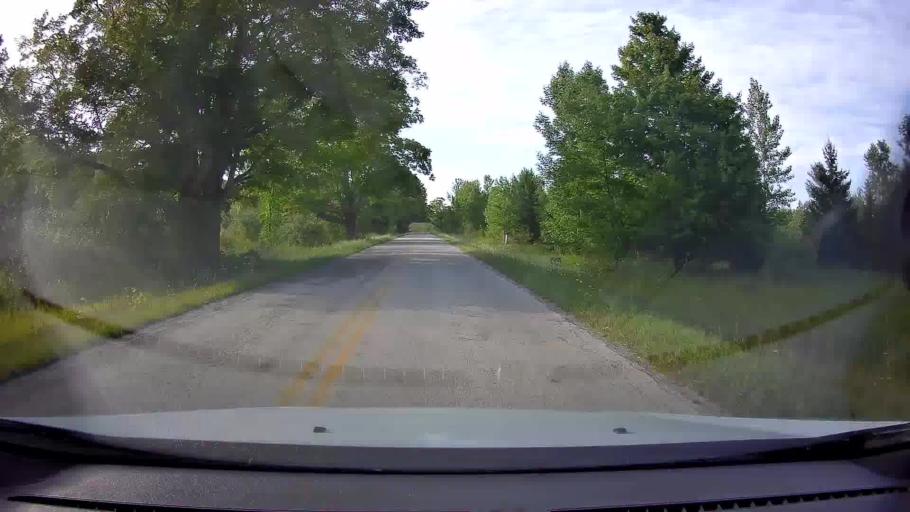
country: US
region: Wisconsin
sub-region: Door County
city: Sturgeon Bay
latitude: 45.1780
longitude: -87.1441
